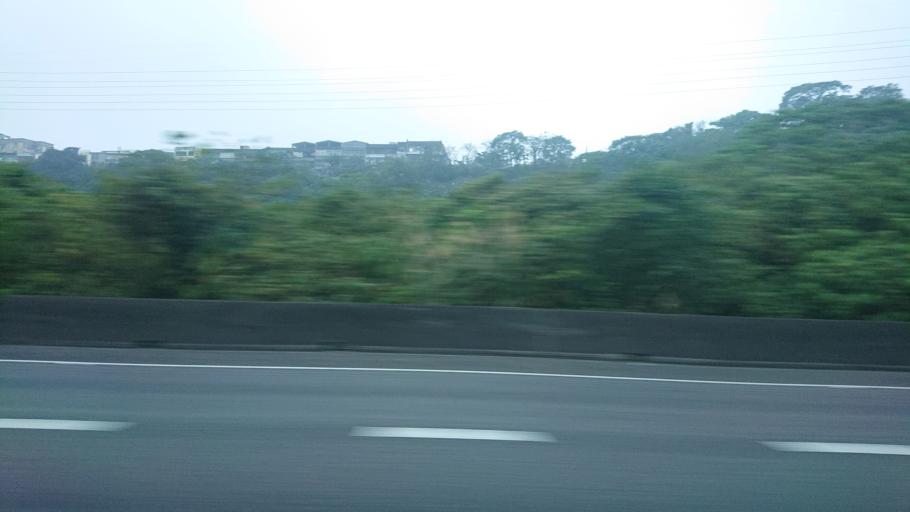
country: TW
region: Taiwan
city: Daxi
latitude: 24.9147
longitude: 121.2941
